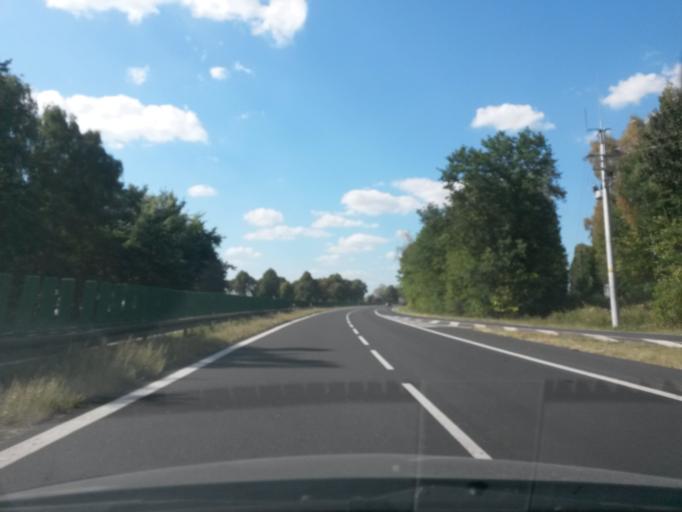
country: PL
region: Masovian Voivodeship
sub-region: Powiat nowodworski
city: Zakroczym
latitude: 52.4532
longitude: 20.5841
